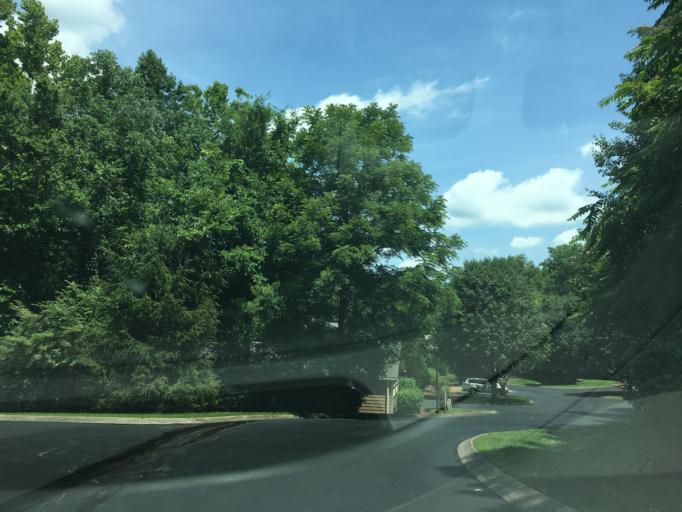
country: US
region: Tennessee
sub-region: Davidson County
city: Belle Meade
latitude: 36.0742
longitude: -86.9103
